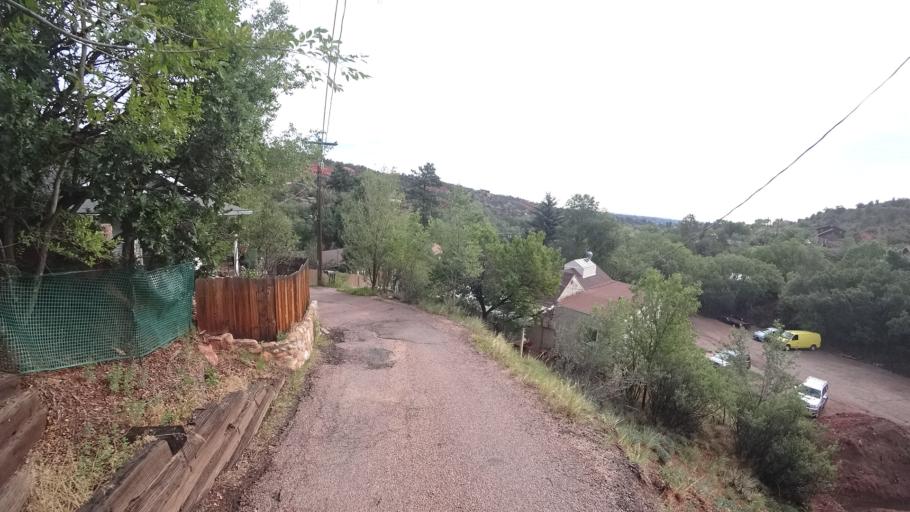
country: US
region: Colorado
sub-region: El Paso County
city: Manitou Springs
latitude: 38.8564
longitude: -104.9099
